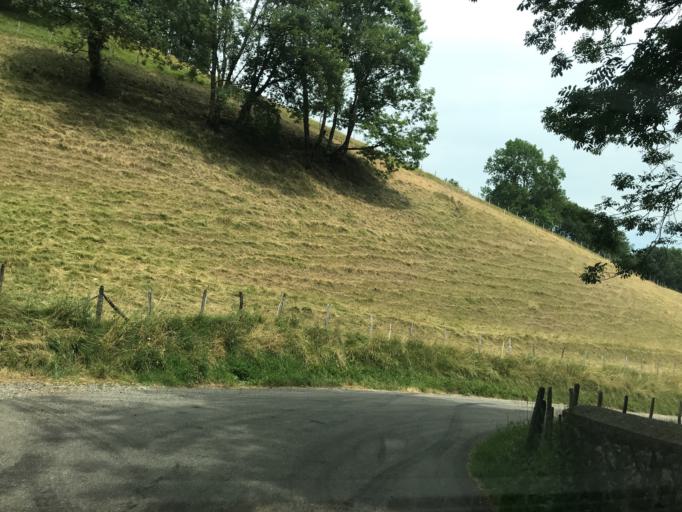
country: FR
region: Rhone-Alpes
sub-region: Departement de l'Isere
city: Barraux
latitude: 45.4499
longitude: 5.9633
